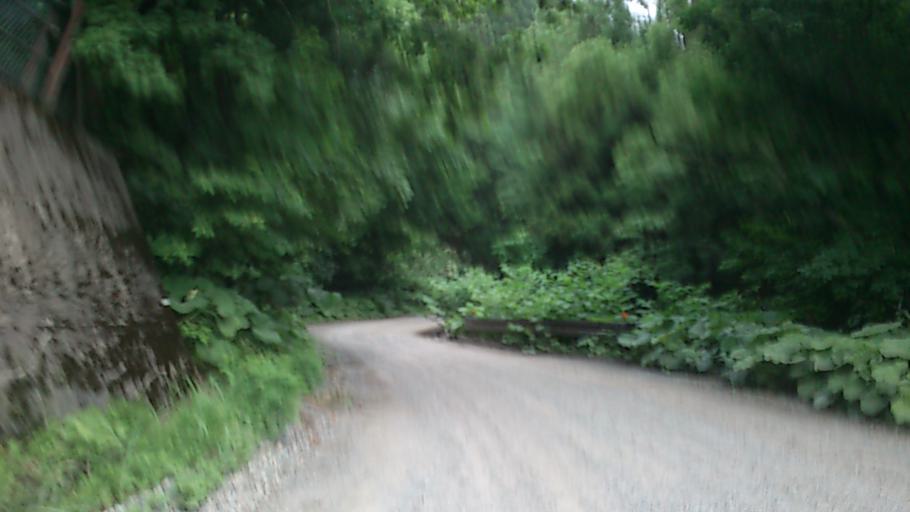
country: JP
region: Aomori
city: Hirosaki
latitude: 40.5245
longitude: 140.1780
